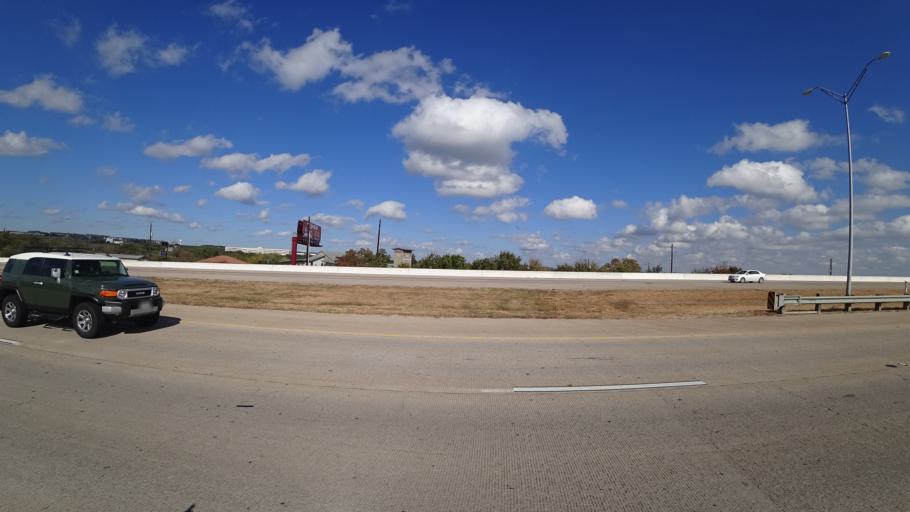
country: US
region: Texas
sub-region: Travis County
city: Barton Creek
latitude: 30.2364
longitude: -97.8416
